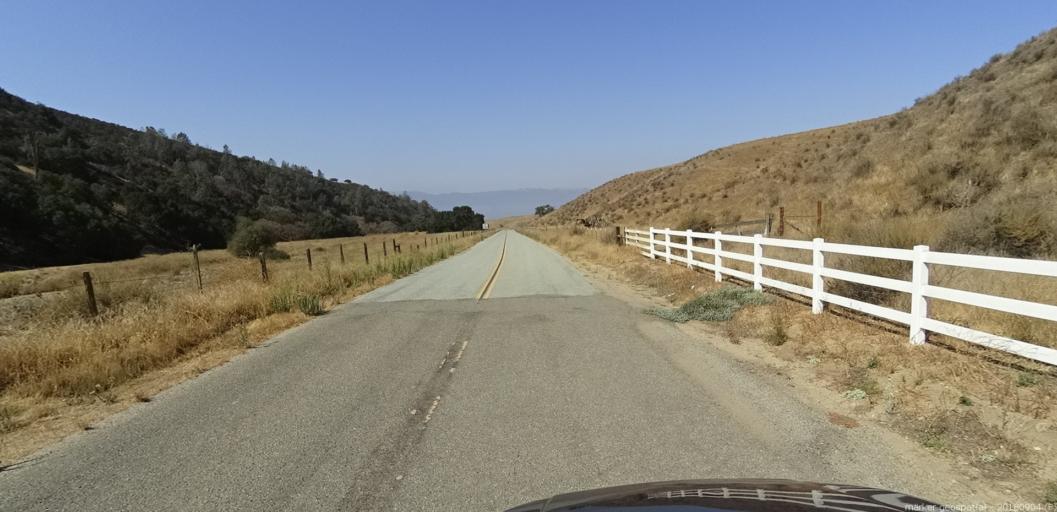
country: US
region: California
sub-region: Monterey County
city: Soledad
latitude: 36.5138
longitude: -121.3427
